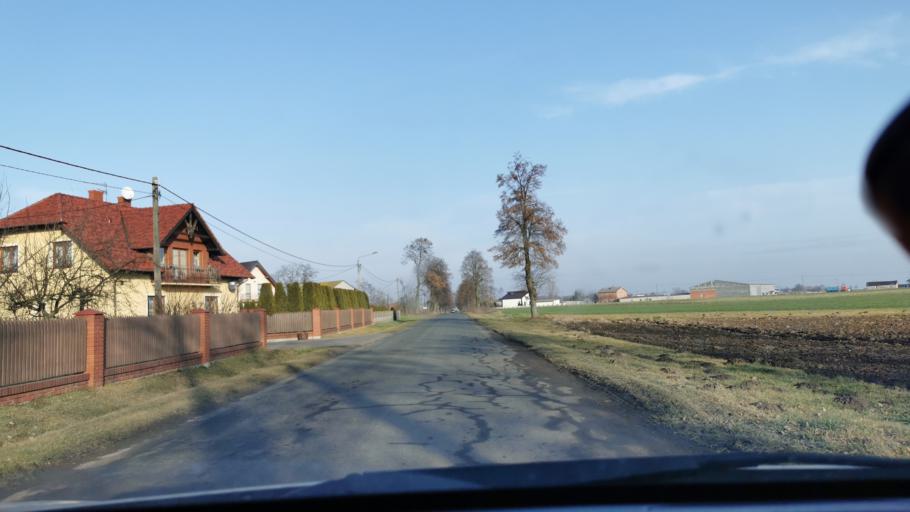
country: PL
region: Greater Poland Voivodeship
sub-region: Powiat kaliski
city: Opatowek
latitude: 51.6792
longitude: 18.3045
